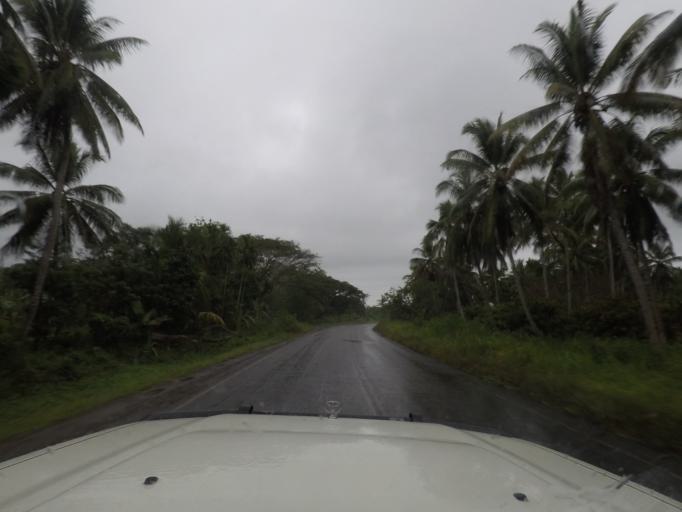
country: PG
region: Madang
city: Madang
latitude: -5.3598
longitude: 145.7103
